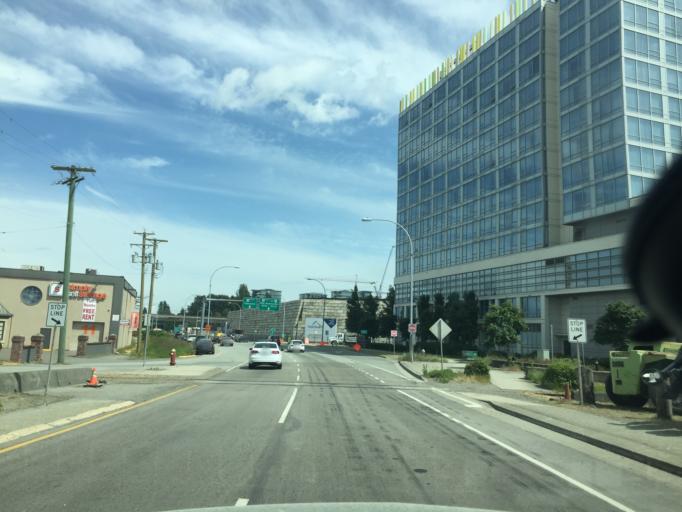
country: CA
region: British Columbia
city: Richmond
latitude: 49.1913
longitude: -123.1345
